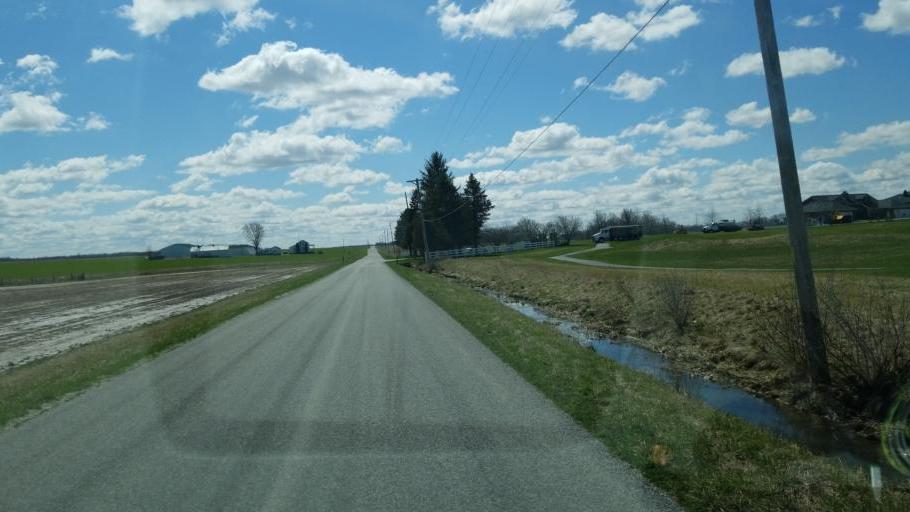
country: US
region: Ohio
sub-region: Seneca County
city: Fostoria
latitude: 41.0643
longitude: -83.5148
